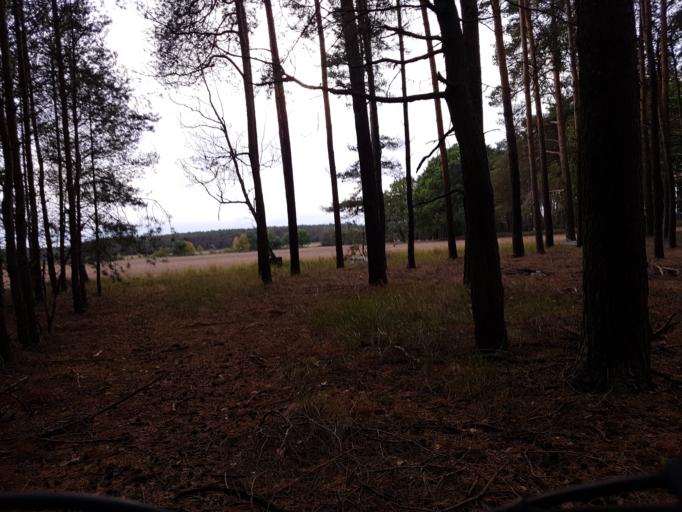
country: DE
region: Brandenburg
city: Schilda
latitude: 51.6092
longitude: 13.3760
